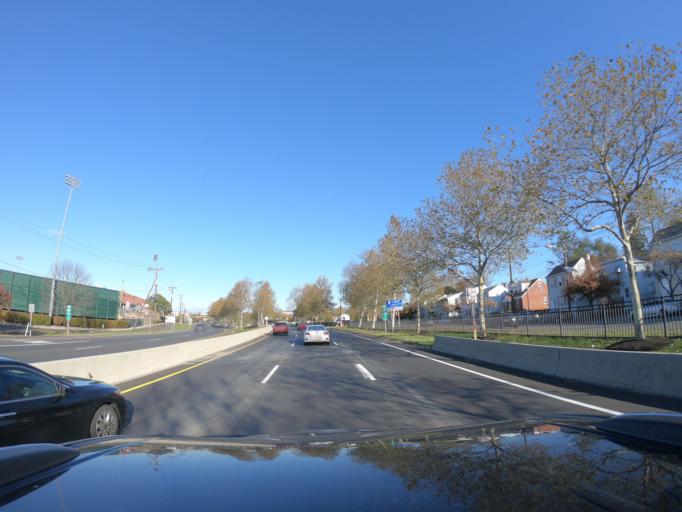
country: US
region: New Jersey
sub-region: Mercer County
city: Trenton
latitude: 40.2032
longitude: -74.7588
